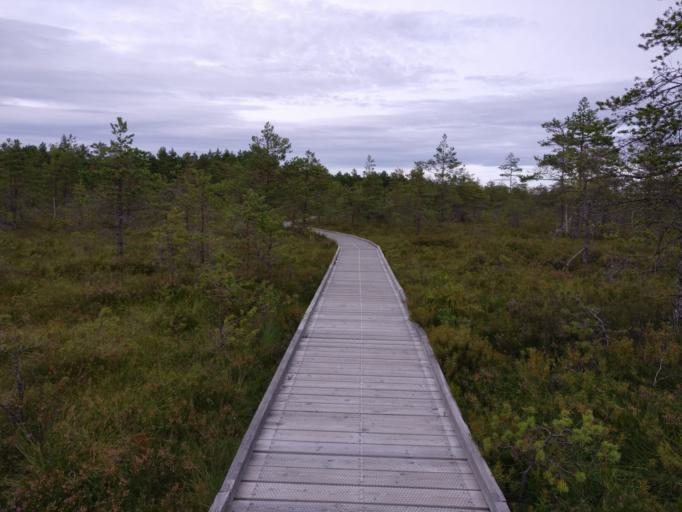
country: EE
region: Paernumaa
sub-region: Vaendra vald (alev)
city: Vandra
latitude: 58.4907
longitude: 24.9831
